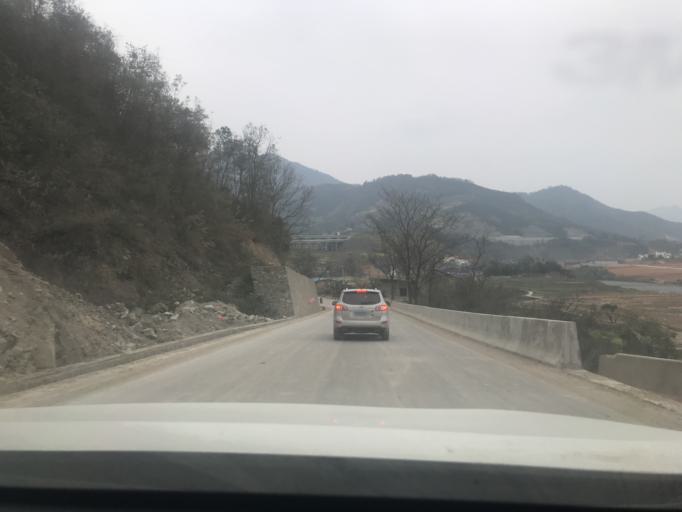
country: CN
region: Guangxi Zhuangzu Zizhiqu
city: Xinzhou
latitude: 25.0172
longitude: 105.8619
